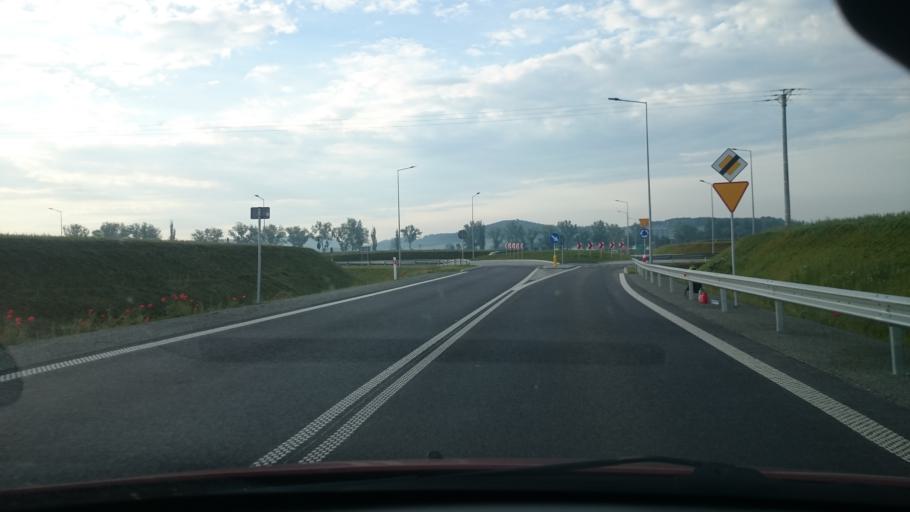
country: PL
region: Lower Silesian Voivodeship
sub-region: Powiat klodzki
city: Klodzko
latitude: 50.3978
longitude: 16.6549
